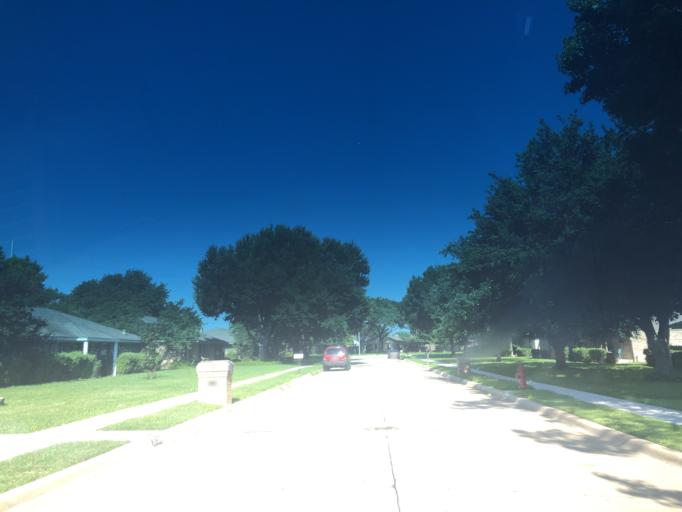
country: US
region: Texas
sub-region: Dallas County
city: Grand Prairie
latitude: 32.7146
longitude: -97.0168
